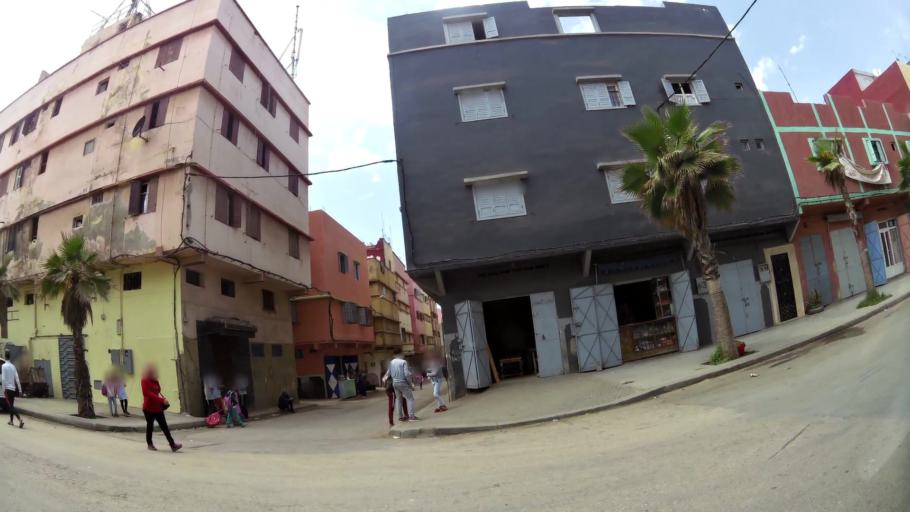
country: MA
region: Rabat-Sale-Zemmour-Zaer
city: Sale
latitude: 34.0501
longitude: -6.8231
